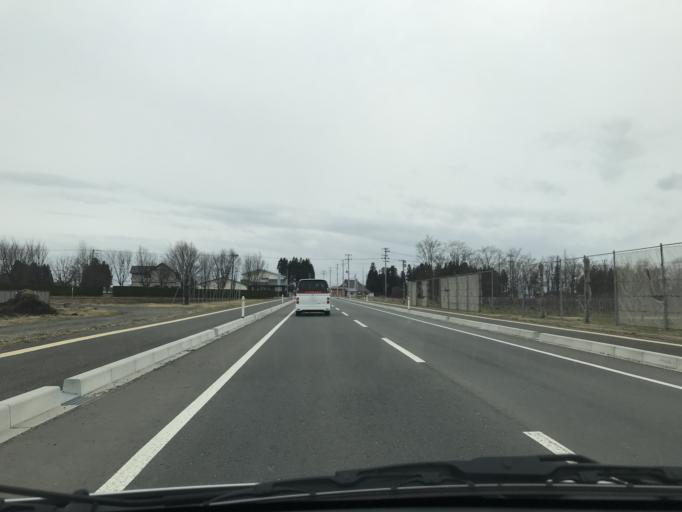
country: JP
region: Iwate
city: Hanamaki
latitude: 39.3533
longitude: 141.1050
